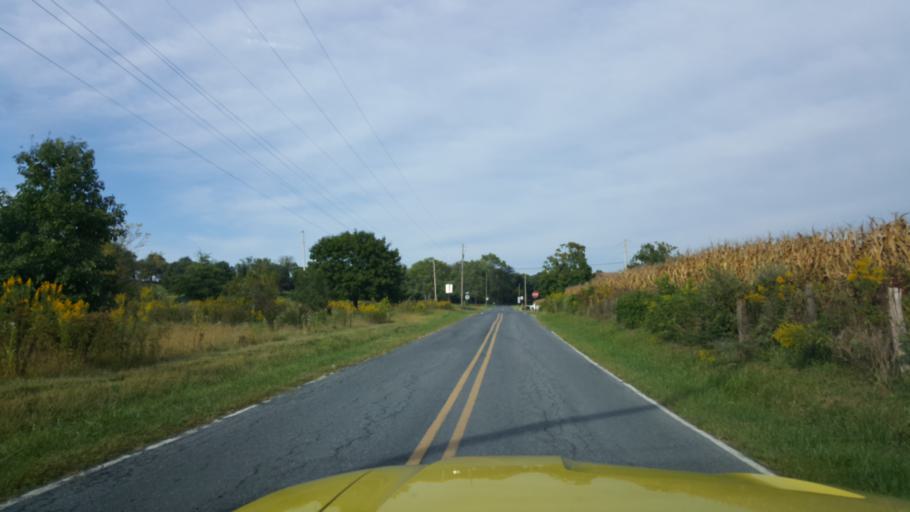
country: US
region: Pennsylvania
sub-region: Lebanon County
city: Campbelltown
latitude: 40.2428
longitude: -76.5641
